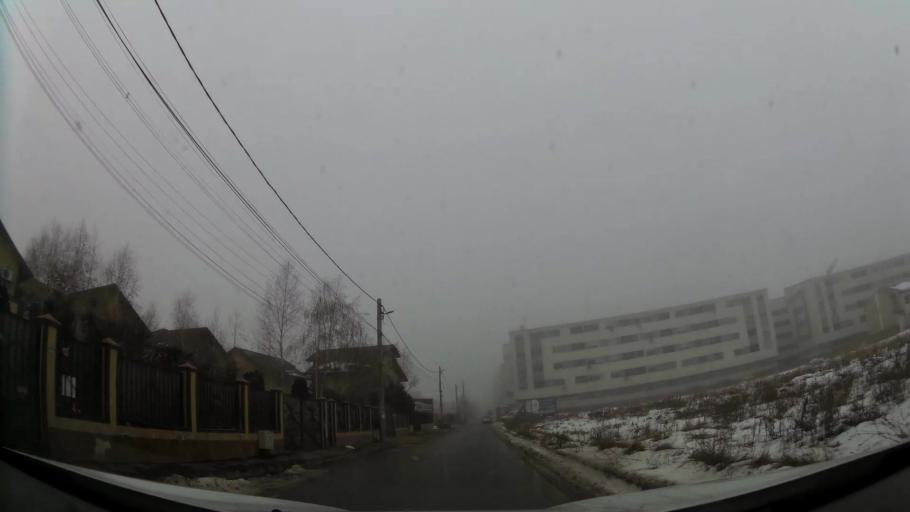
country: RO
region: Ilfov
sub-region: Comuna Chiajna
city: Chiajna
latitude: 44.4521
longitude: 25.9855
